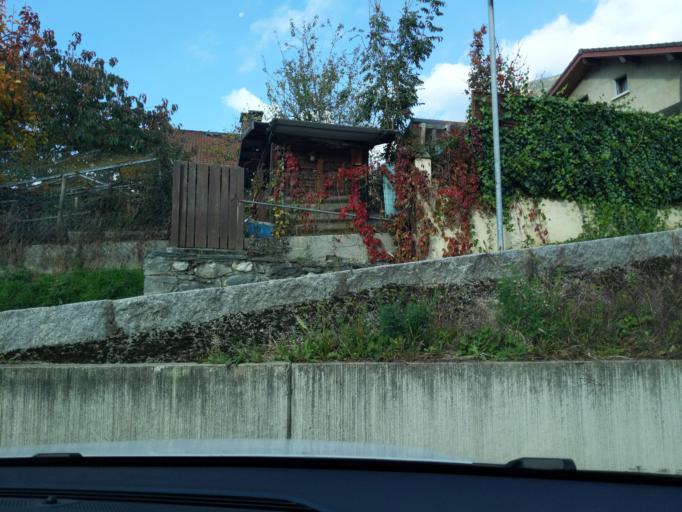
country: FR
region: Rhone-Alpes
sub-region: Departement de la Savoie
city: Aime
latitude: 45.5583
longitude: 6.6546
